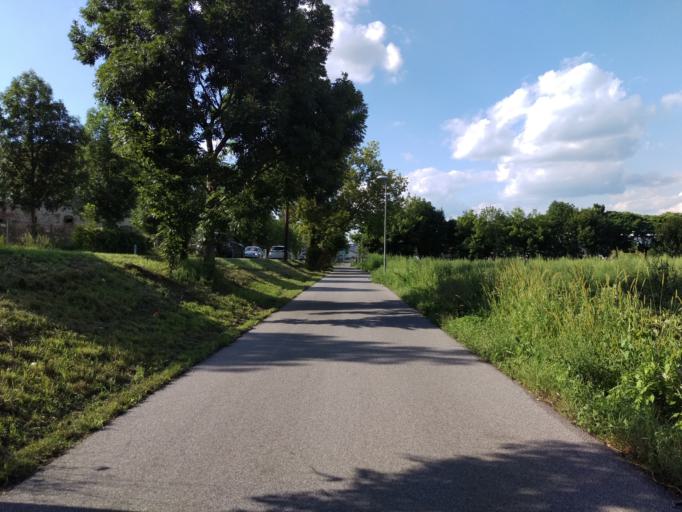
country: AT
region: Styria
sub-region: Graz Stadt
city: Wetzelsdorf
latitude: 47.0637
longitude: 15.4123
